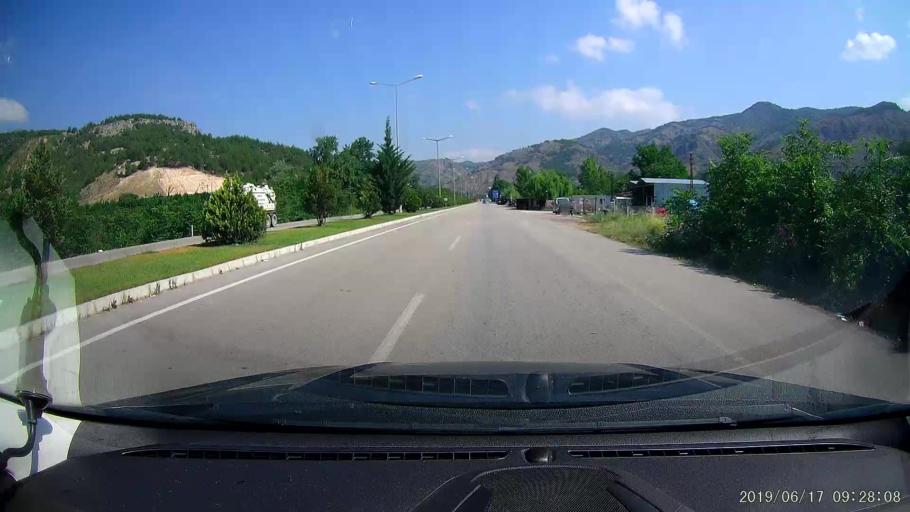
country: TR
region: Amasya
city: Amasya
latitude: 40.6848
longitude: 35.8231
